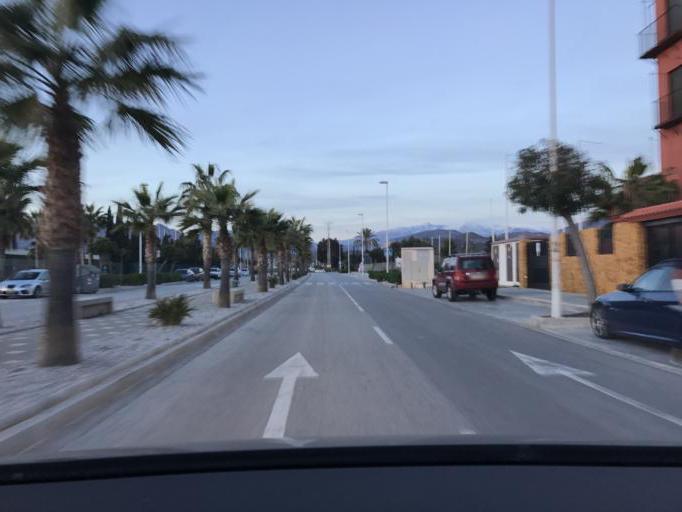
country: ES
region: Andalusia
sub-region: Provincia de Granada
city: Salobrena
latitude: 36.7221
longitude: -3.5595
